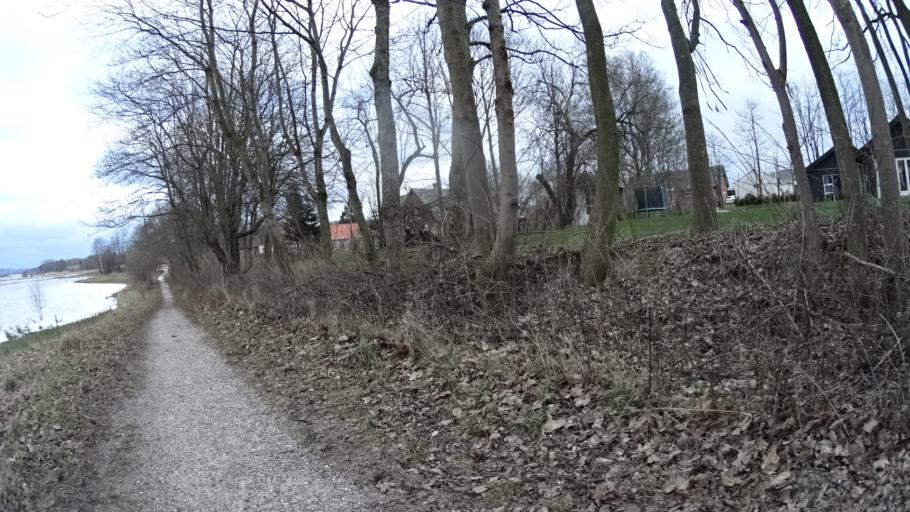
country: DK
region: Central Jutland
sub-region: Arhus Kommune
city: Kolt
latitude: 56.1272
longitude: 10.0483
